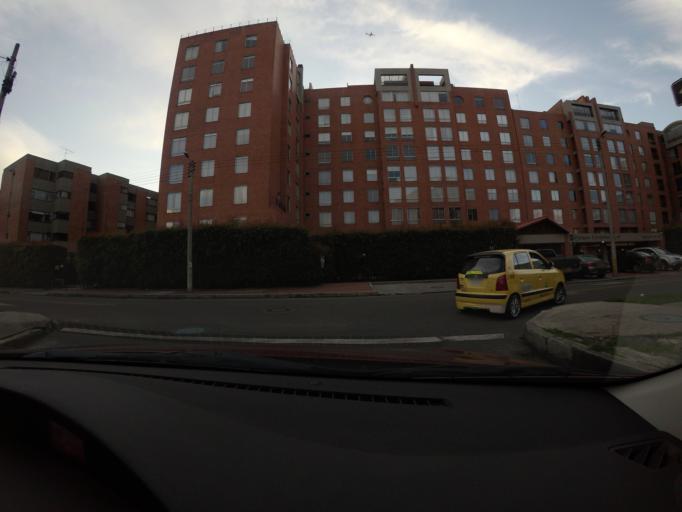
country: CO
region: Bogota D.C.
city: Barrio San Luis
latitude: 4.7074
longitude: -74.0628
